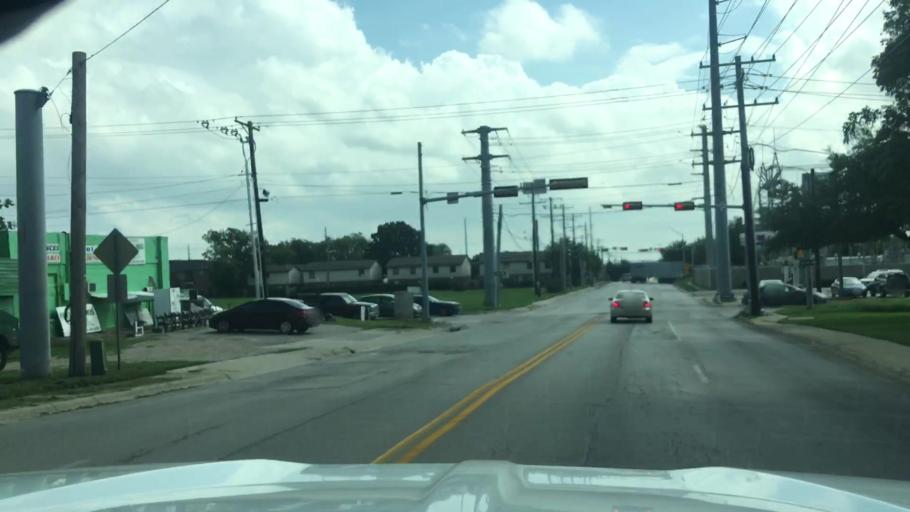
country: US
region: Texas
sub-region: Denton County
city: Denton
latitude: 33.2163
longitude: -97.1614
